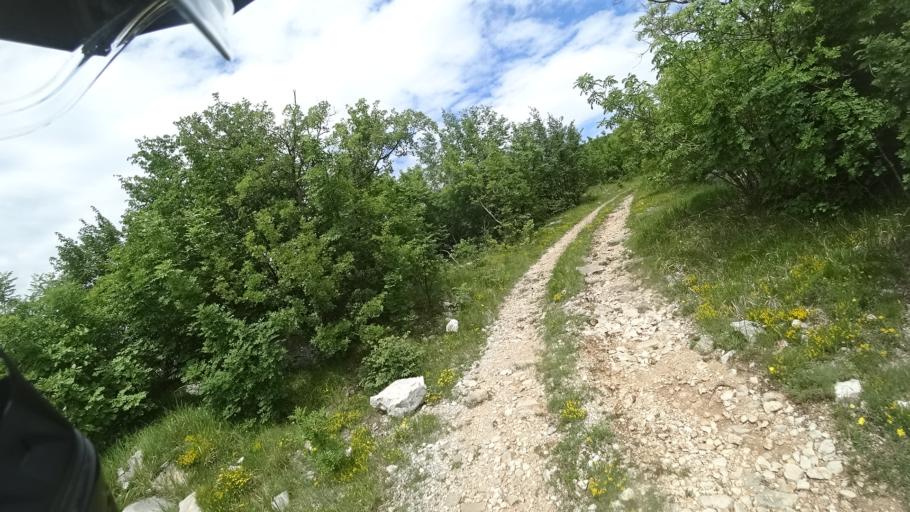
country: HR
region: Splitsko-Dalmatinska
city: Hrvace
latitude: 43.8834
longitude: 16.5825
